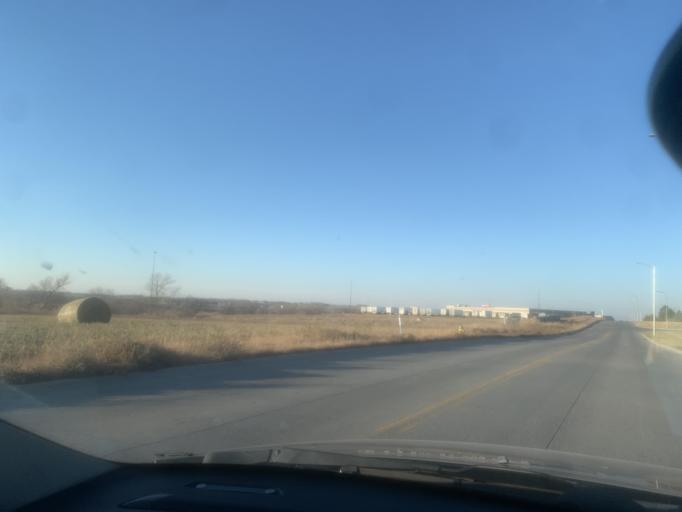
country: US
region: Nebraska
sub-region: Sarpy County
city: Chalco
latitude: 41.1396
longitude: -96.1580
